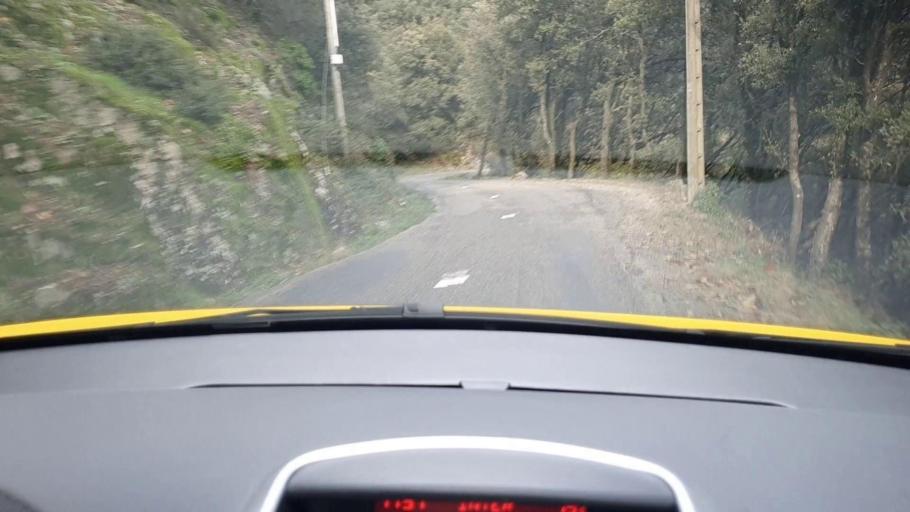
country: FR
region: Languedoc-Roussillon
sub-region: Departement du Gard
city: Lasalle
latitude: 44.0899
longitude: 3.8014
